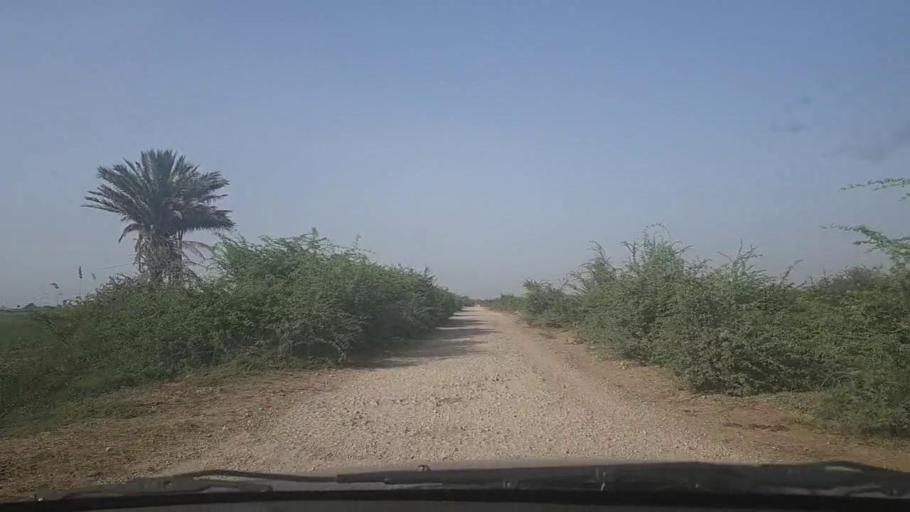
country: PK
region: Sindh
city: Keti Bandar
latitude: 24.2508
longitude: 67.5613
